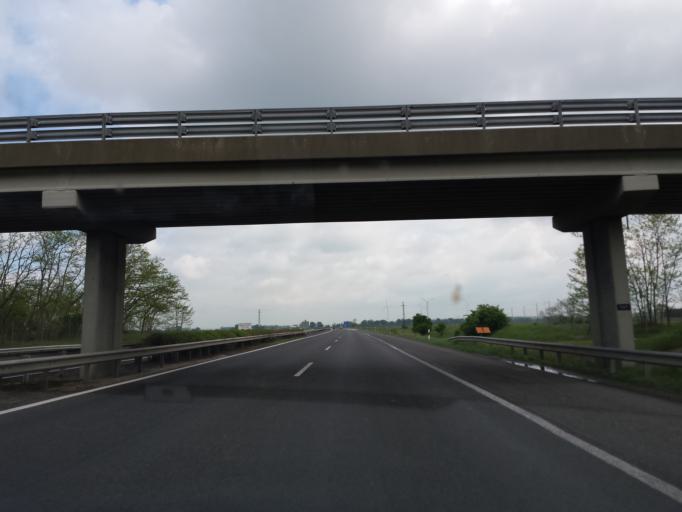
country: HU
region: Gyor-Moson-Sopron
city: Bony
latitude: 47.6857
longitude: 17.8192
